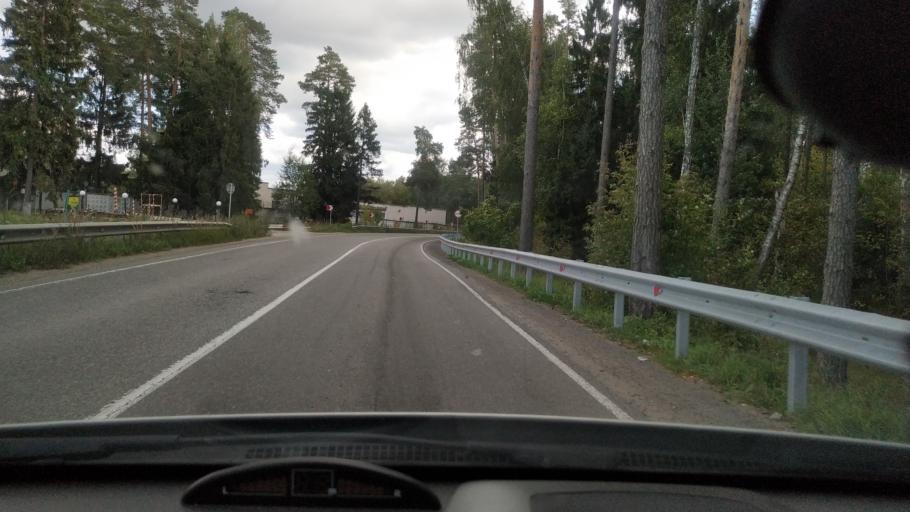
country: RU
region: Moskovskaya
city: Zheleznodorozhnyy
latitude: 55.7921
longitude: 38.0349
